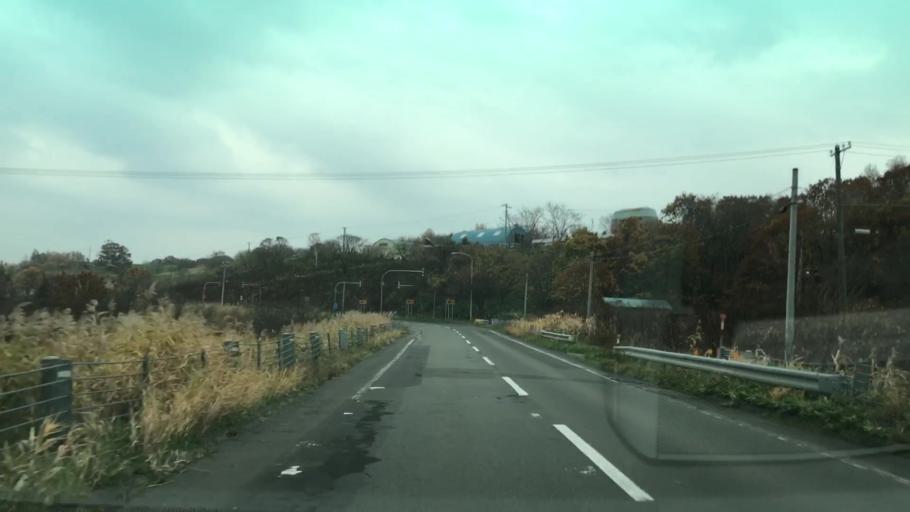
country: JP
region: Hokkaido
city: Ishikari
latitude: 43.3350
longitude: 141.4291
